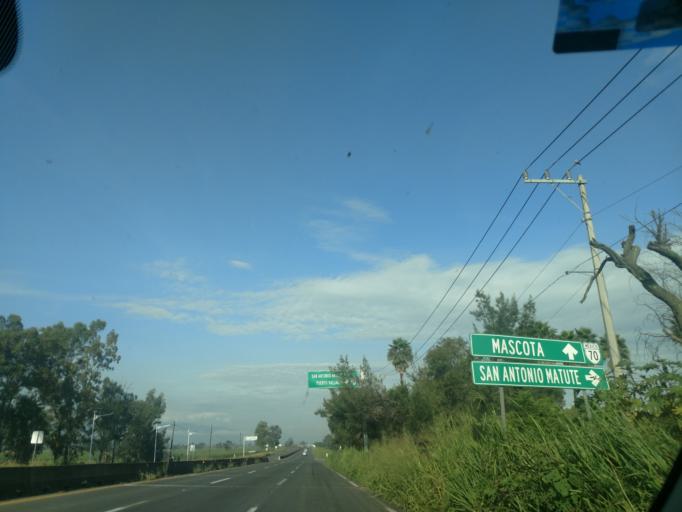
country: MX
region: Jalisco
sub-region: Ameca
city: Los Pocitos
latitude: 20.5363
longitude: -103.9455
